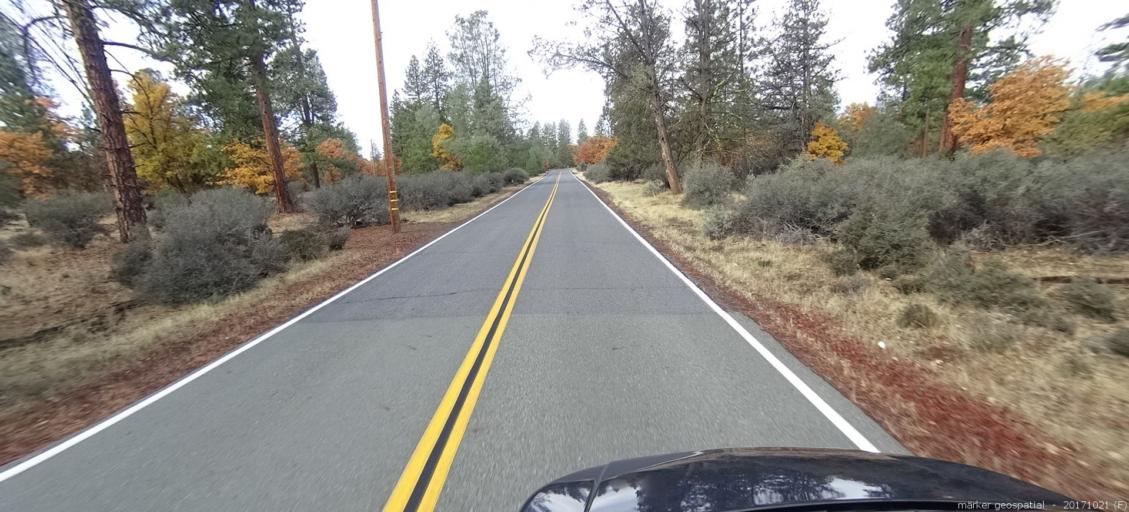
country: US
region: California
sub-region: Shasta County
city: Burney
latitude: 40.9183
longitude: -121.5428
